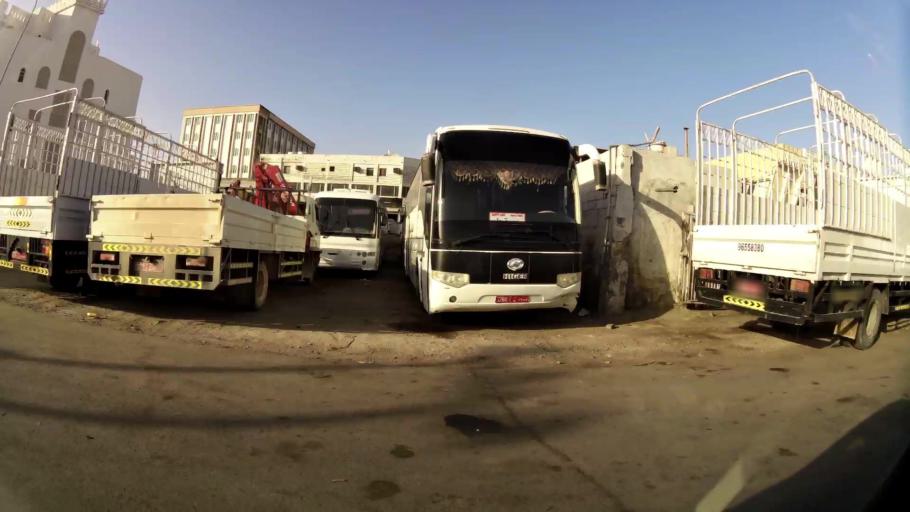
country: OM
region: Muhafazat Masqat
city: Muscat
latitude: 23.5863
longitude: 58.5550
